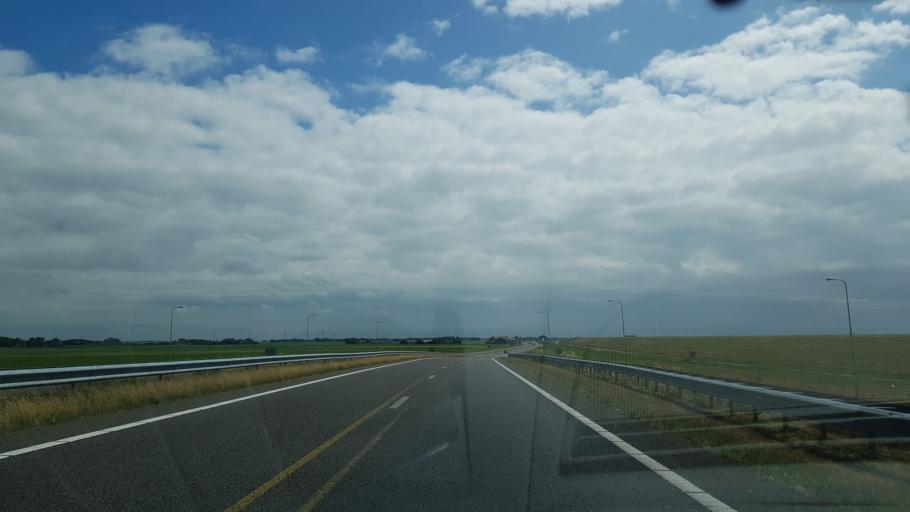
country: NL
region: Friesland
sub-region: Gemeente Harlingen
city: Harlingen
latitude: 53.1460
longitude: 5.4131
